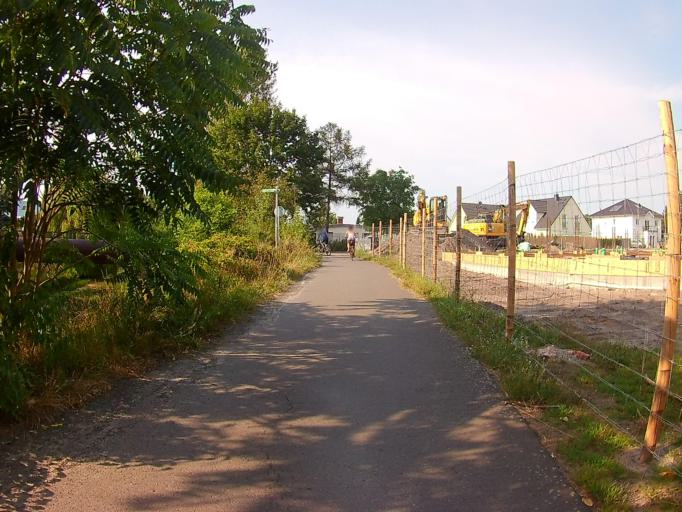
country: DE
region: Berlin
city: Kopenick Bezirk
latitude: 52.4750
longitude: 13.5679
